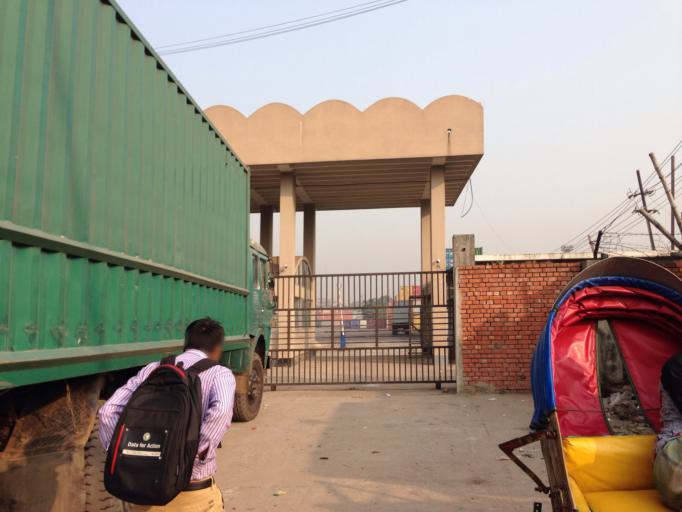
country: BD
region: Dhaka
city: Paltan
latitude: 23.7252
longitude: 90.4270
